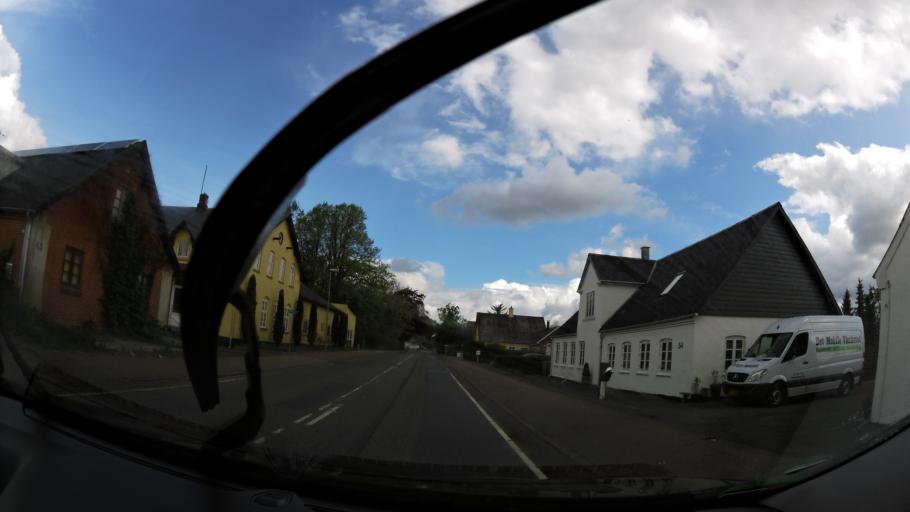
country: DK
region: South Denmark
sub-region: Svendborg Kommune
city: Thuro By
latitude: 55.1067
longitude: 10.7137
